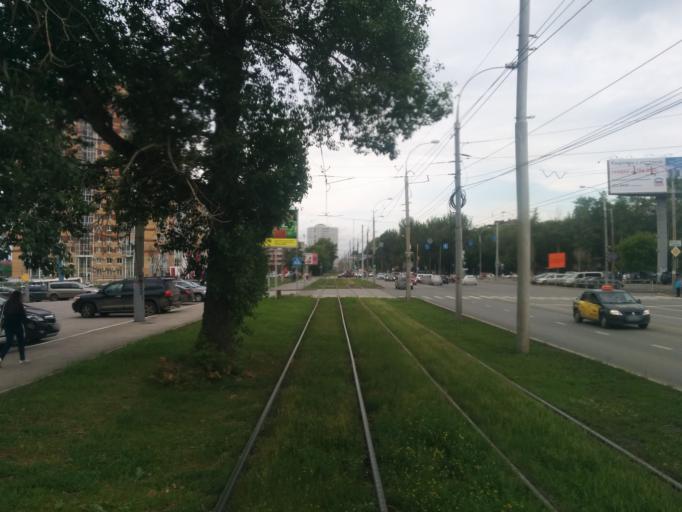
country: RU
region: Perm
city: Perm
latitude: 58.0058
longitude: 56.2848
